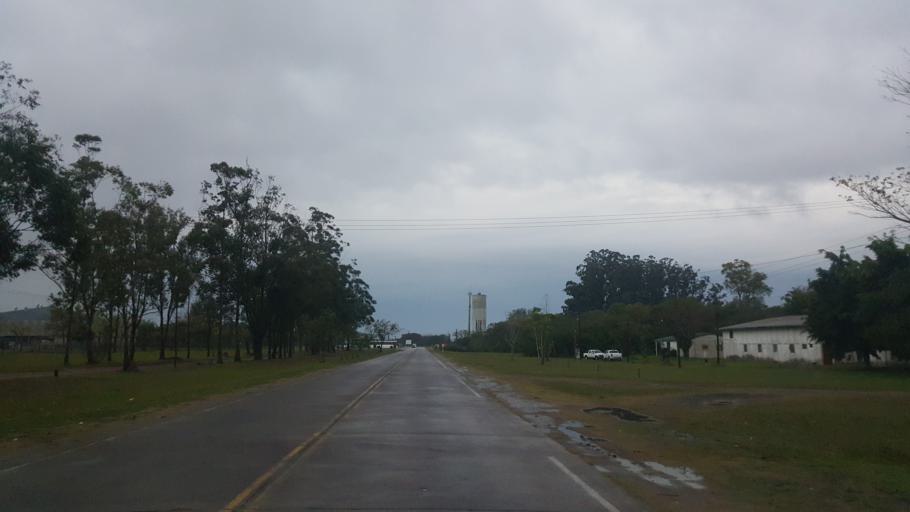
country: AR
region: Corrientes
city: Ituzaingo
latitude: -27.5812
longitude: -56.6758
